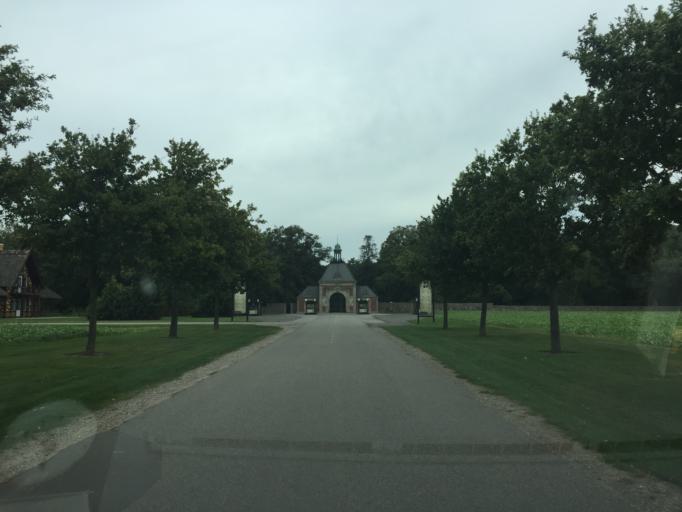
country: DK
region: Zealand
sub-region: Lolland Kommune
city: Maribo
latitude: 54.8100
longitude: 11.5104
